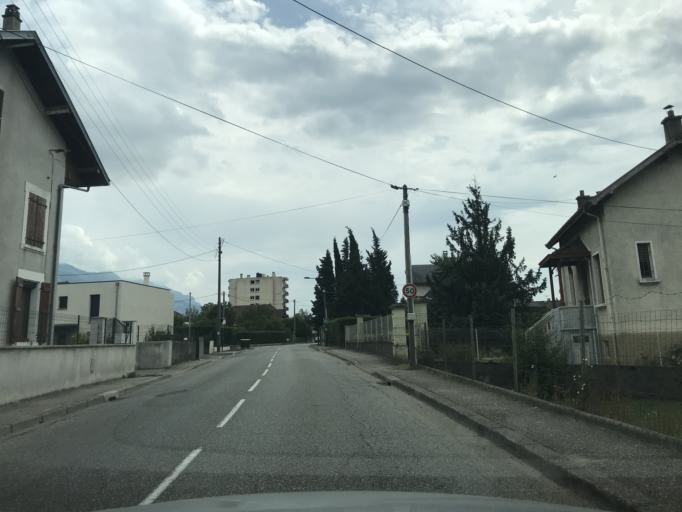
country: FR
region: Rhone-Alpes
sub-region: Departement de la Savoie
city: Brison-Saint-Innocent
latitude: 45.7065
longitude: 5.8941
